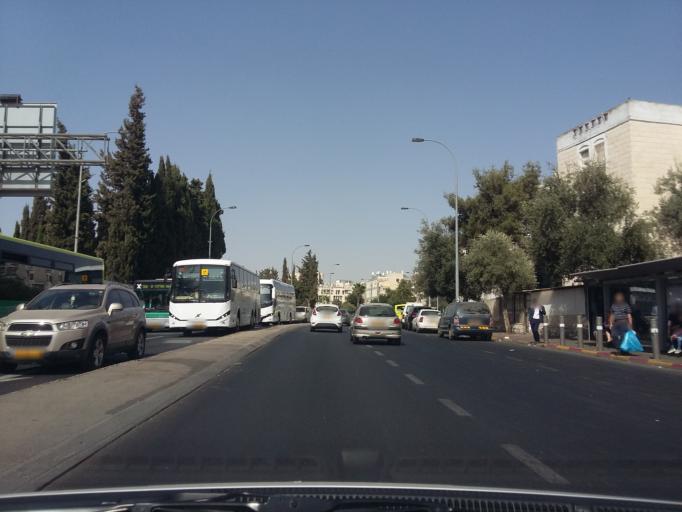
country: IL
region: Jerusalem
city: West Jerusalem
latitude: 31.7960
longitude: 35.2205
